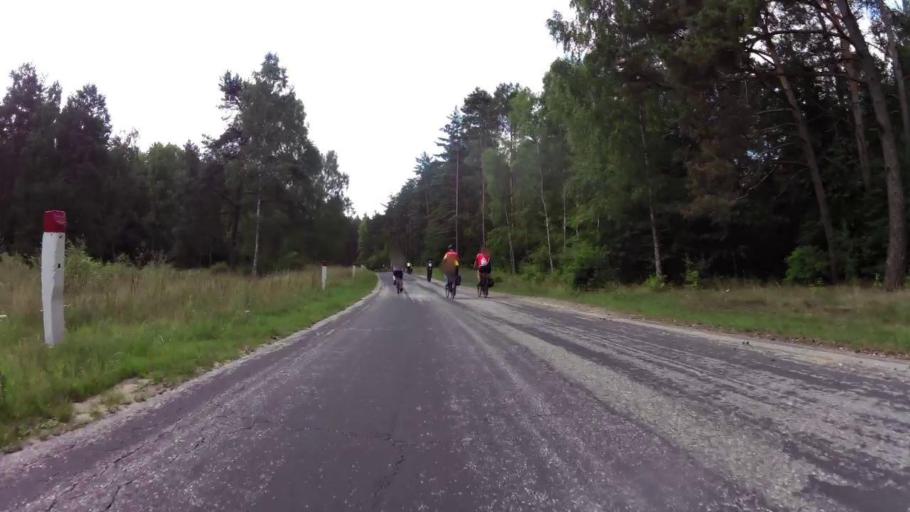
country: PL
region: West Pomeranian Voivodeship
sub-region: Powiat drawski
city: Drawsko Pomorskie
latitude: 53.4646
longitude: 15.7774
